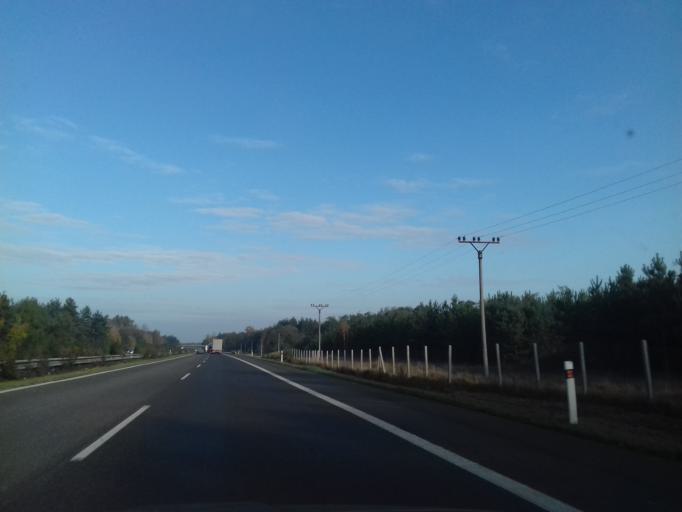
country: SK
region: Bratislavsky
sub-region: Okres Malacky
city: Malacky
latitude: 48.4537
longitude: 17.0406
